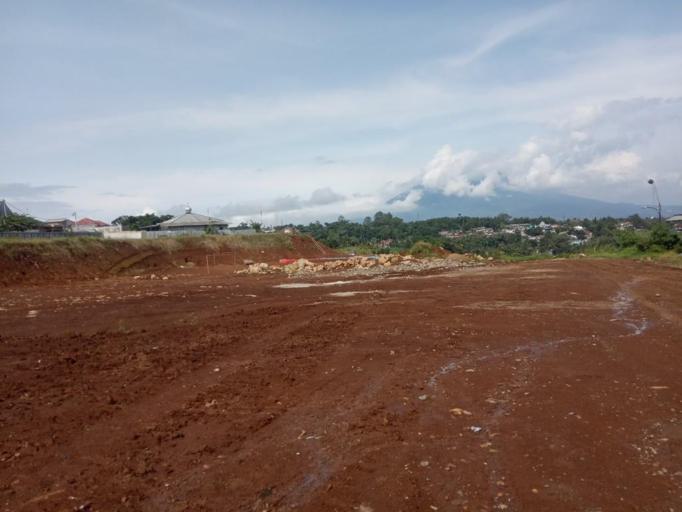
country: ID
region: West Java
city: Caringin
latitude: -6.6601
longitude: 106.8808
